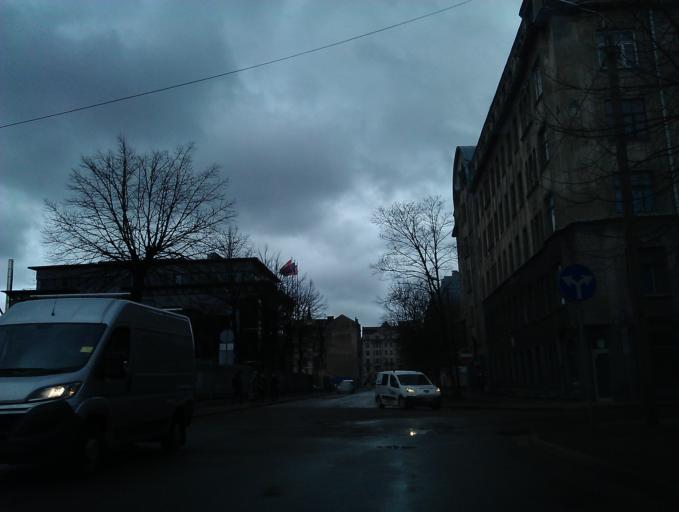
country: LV
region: Riga
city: Riga
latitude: 56.9609
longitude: 24.1146
